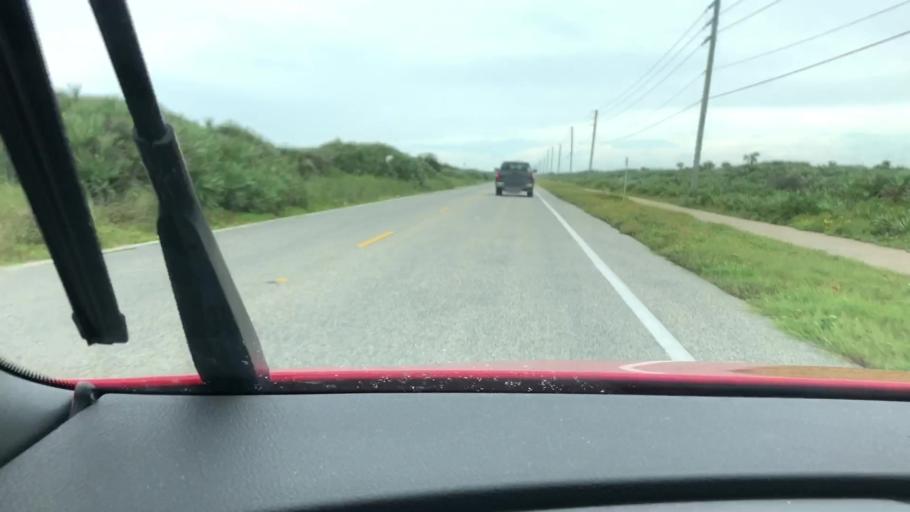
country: US
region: Florida
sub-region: Flagler County
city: Flagler Beach
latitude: 29.4175
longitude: -81.0982
